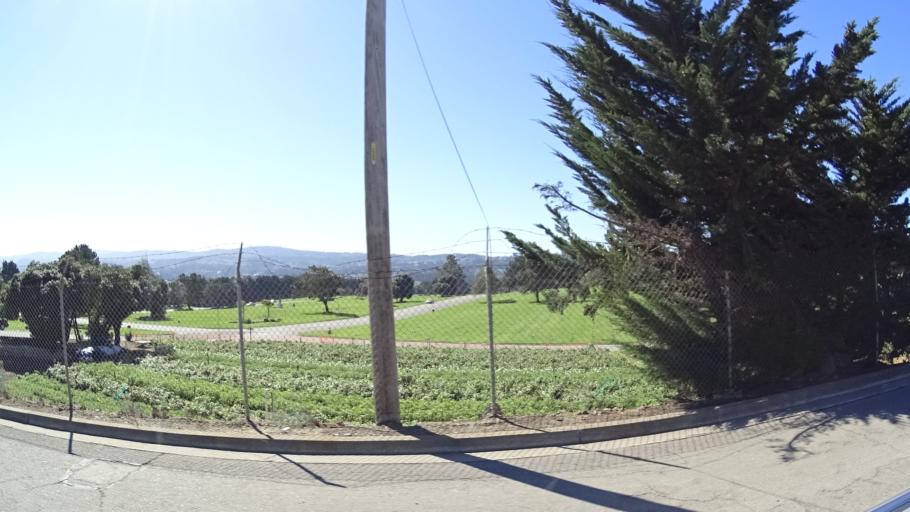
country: US
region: California
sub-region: San Mateo County
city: Colma
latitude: 37.6716
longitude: -122.4390
